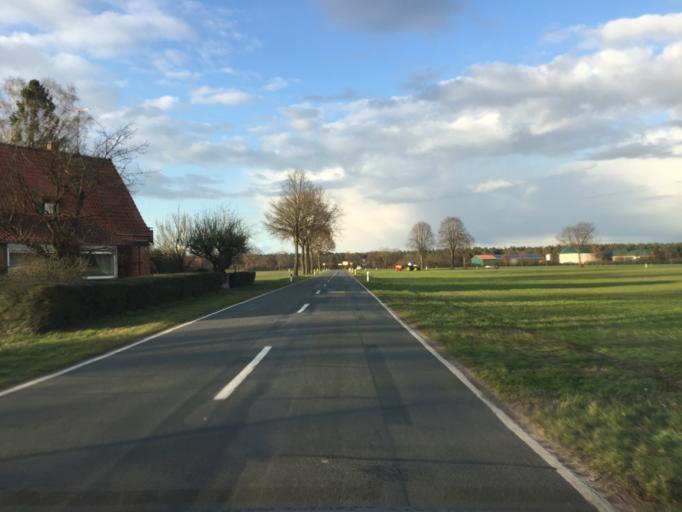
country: DE
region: Lower Saxony
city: Steyerberg
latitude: 52.5894
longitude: 8.9801
